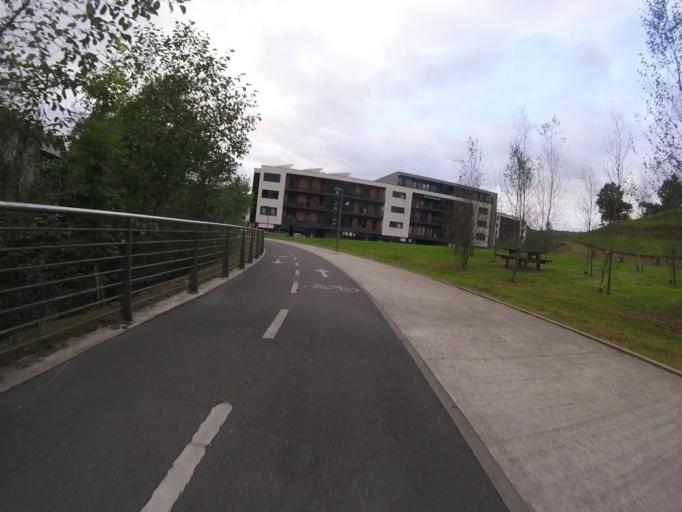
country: ES
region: Basque Country
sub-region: Provincia de Guipuzcoa
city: Errenteria
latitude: 43.2910
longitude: -1.8553
